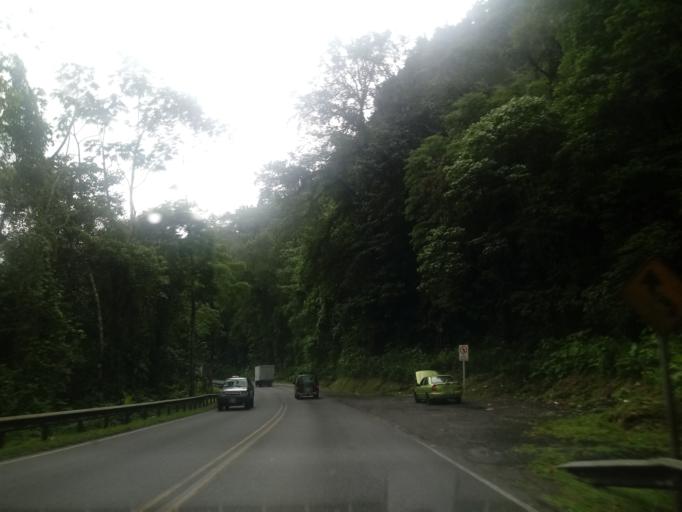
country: CR
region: San Jose
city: Dulce Nombre de Jesus
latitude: 10.1474
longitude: -83.9461
